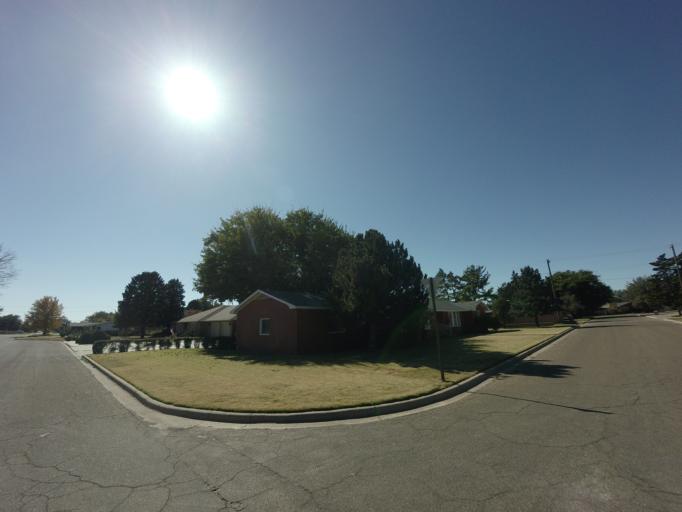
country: US
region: New Mexico
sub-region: Curry County
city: Clovis
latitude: 34.4209
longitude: -103.1990
